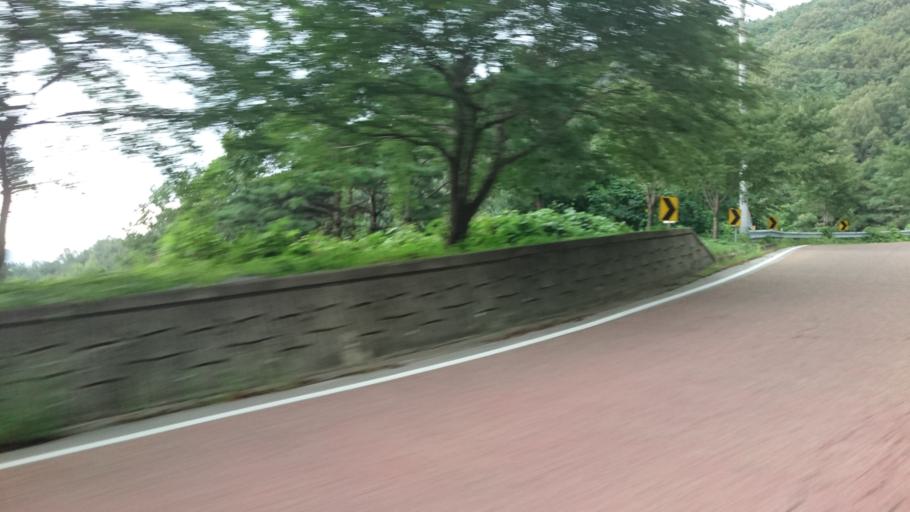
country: KR
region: Daegu
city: Daegu
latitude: 36.0214
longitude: 128.5654
